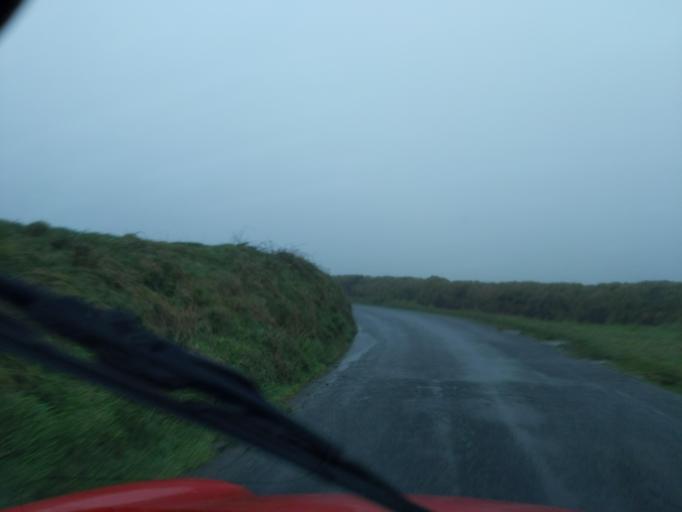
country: GB
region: England
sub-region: Cornwall
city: Camelford
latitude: 50.6532
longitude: -4.7018
